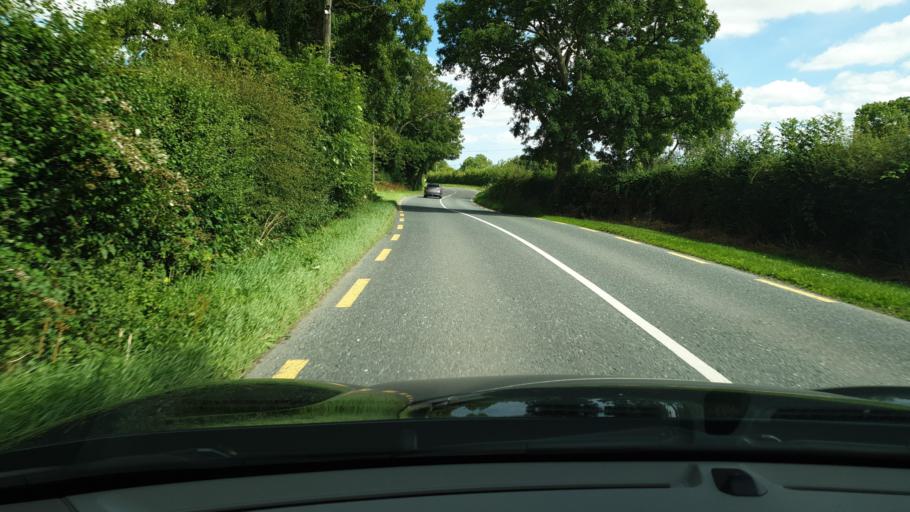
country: IE
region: Leinster
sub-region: Kildare
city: Maynooth
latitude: 53.4378
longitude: -6.5411
